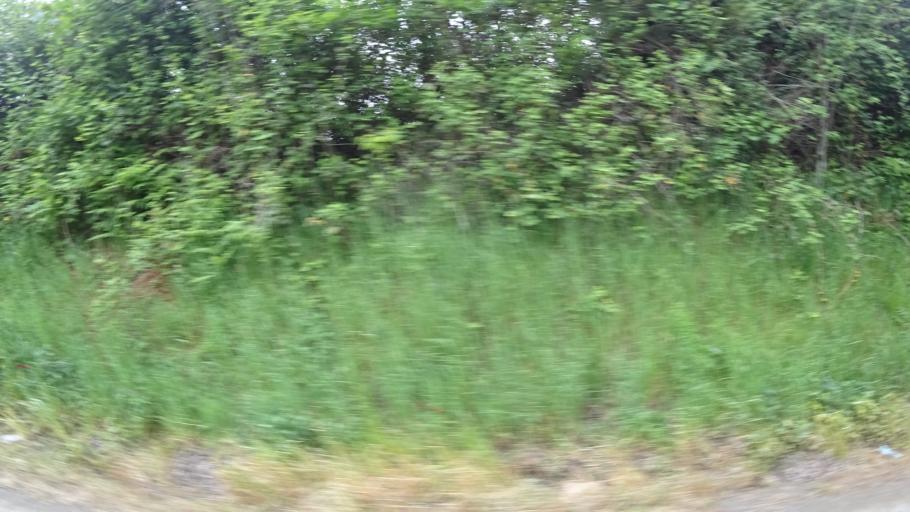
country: US
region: Oregon
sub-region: Washington County
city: Hillsboro
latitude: 45.4836
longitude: -122.9831
